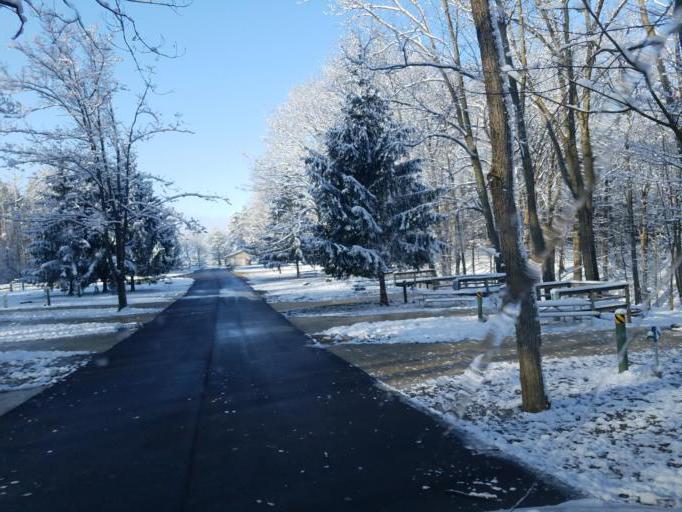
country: US
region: Ohio
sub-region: Morrow County
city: Mount Gilead
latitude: 40.5482
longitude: -82.8095
